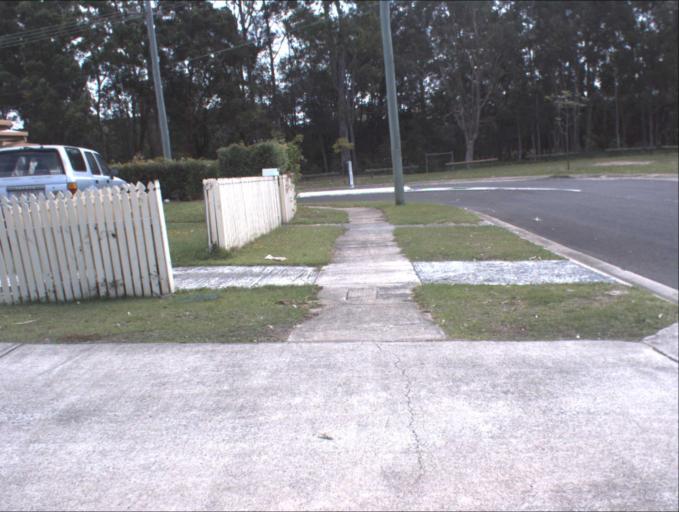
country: AU
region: Queensland
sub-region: Logan
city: Logan Reserve
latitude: -27.6854
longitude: 153.0798
